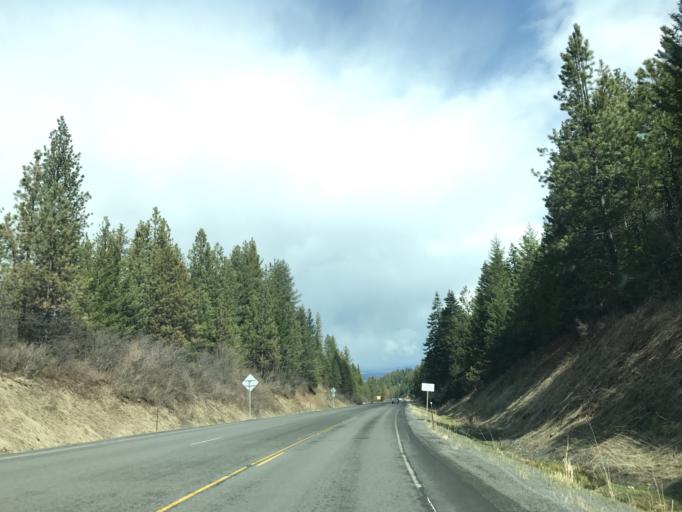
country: US
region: Idaho
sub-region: Idaho County
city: Grangeville
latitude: 45.8481
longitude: -116.2394
